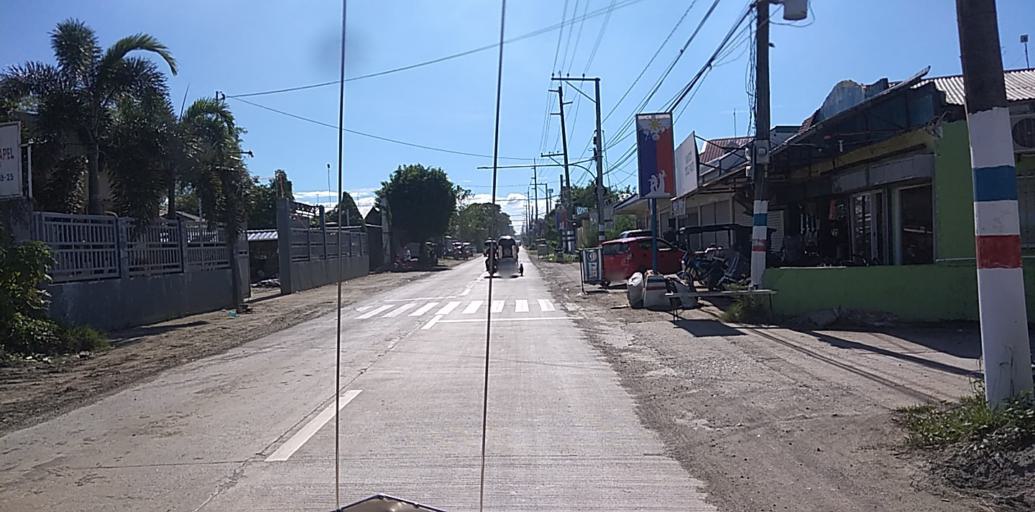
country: PH
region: Central Luzon
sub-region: Province of Pampanga
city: San Luis
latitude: 15.0511
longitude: 120.7822
